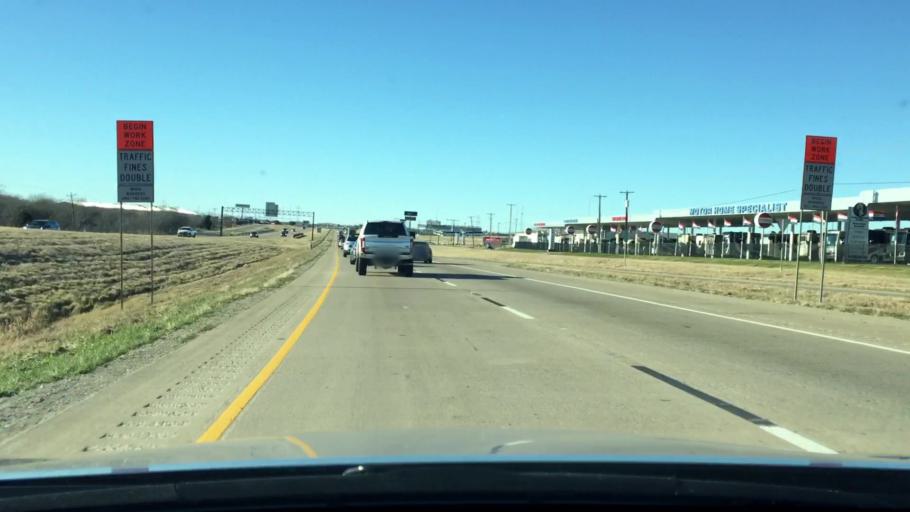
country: US
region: Texas
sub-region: Johnson County
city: Alvarado
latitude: 32.4229
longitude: -97.2301
